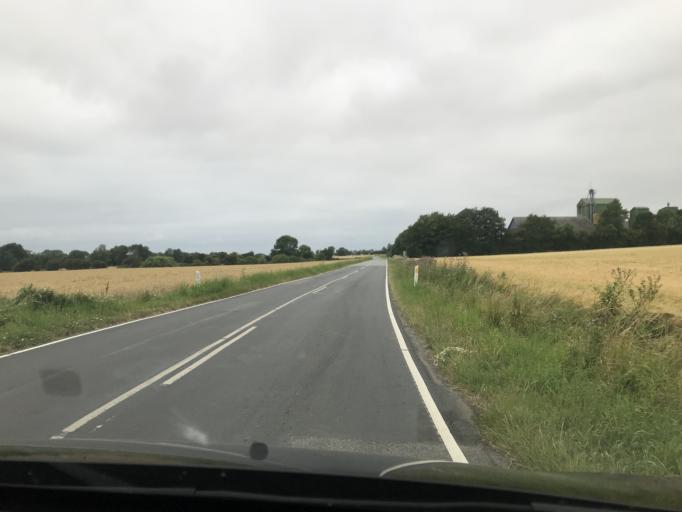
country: DK
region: South Denmark
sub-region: AEro Kommune
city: AEroskobing
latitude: 54.8569
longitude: 10.3950
